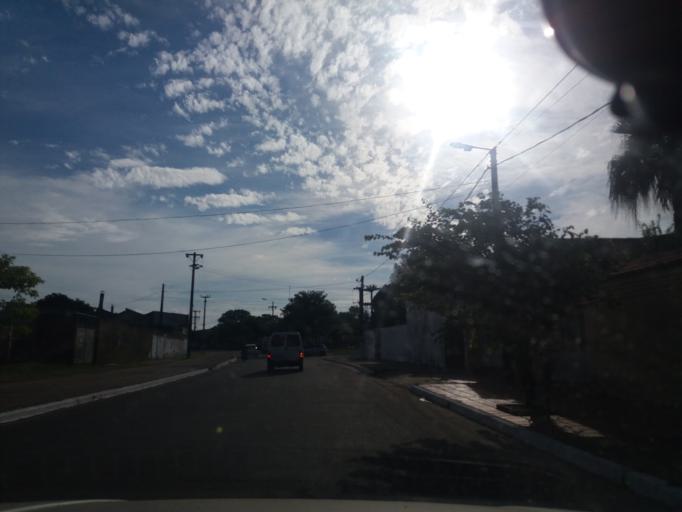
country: AR
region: Corrientes
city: Corrientes
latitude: -27.4825
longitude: -58.8276
